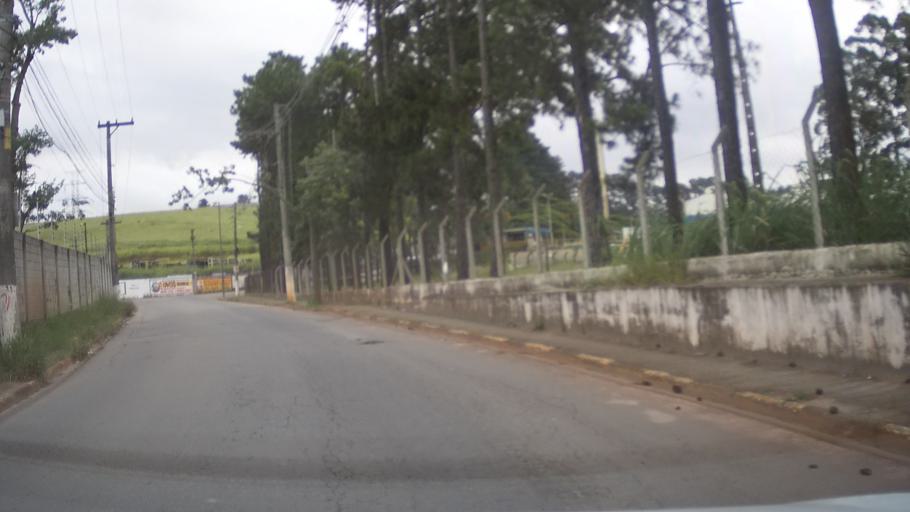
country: BR
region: Sao Paulo
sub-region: Itaquaquecetuba
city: Itaquaquecetuba
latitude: -23.4496
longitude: -46.3793
